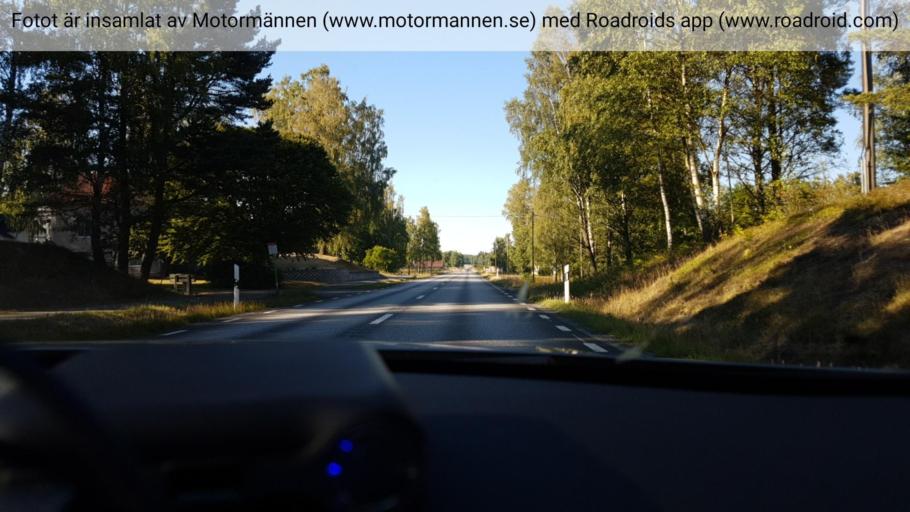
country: SE
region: Joenkoeping
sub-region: Habo Kommun
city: Habo
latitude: 58.0403
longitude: 14.1800
